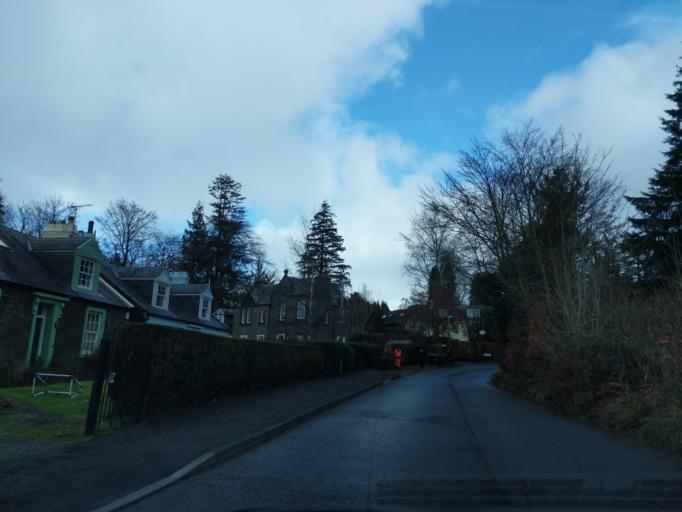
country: GB
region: Scotland
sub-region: Dumfries and Galloway
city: Moffat
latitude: 55.3343
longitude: -3.4373
